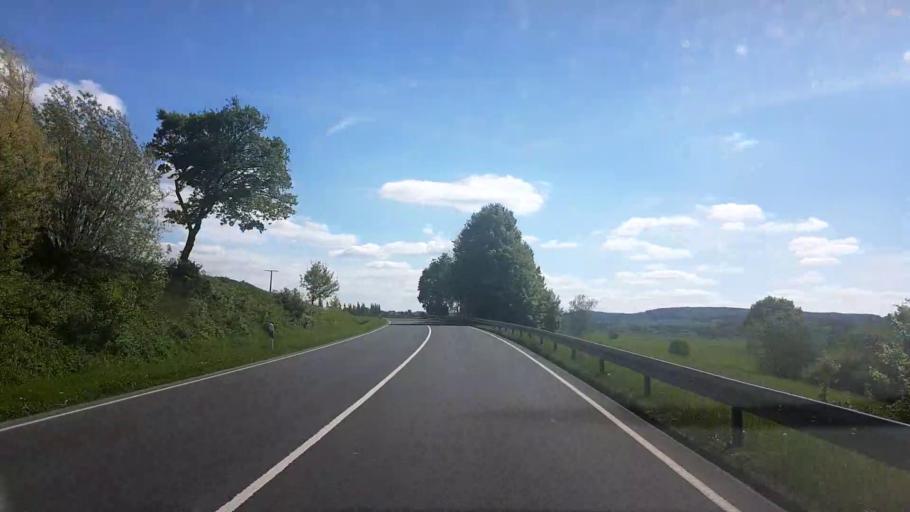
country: DE
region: Bavaria
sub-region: Regierungsbezirk Unterfranken
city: Untermerzbach
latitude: 50.1138
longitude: 10.8686
